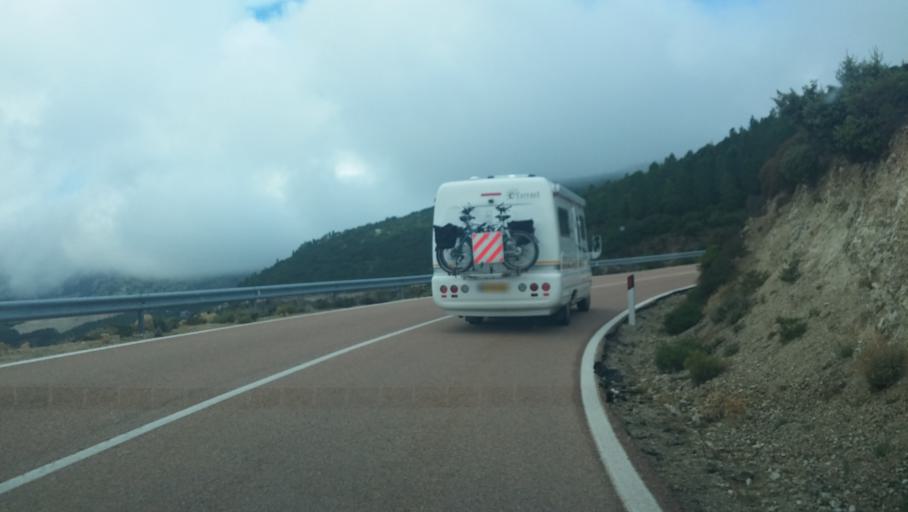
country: IT
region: Sardinia
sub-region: Provincia di Ogliastra
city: Urzulei
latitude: 40.1627
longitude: 9.5269
